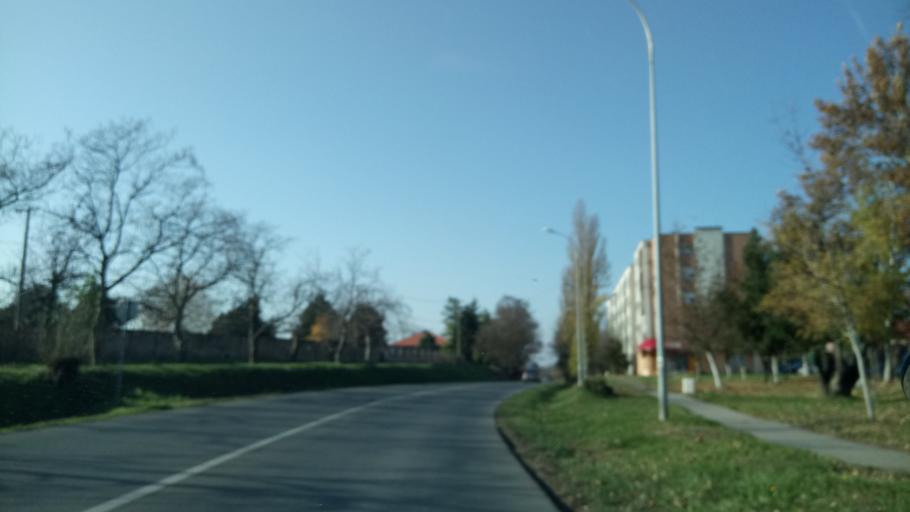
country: RS
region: Autonomna Pokrajina Vojvodina
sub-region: Sremski Okrug
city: Ingija
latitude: 45.0527
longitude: 20.0721
